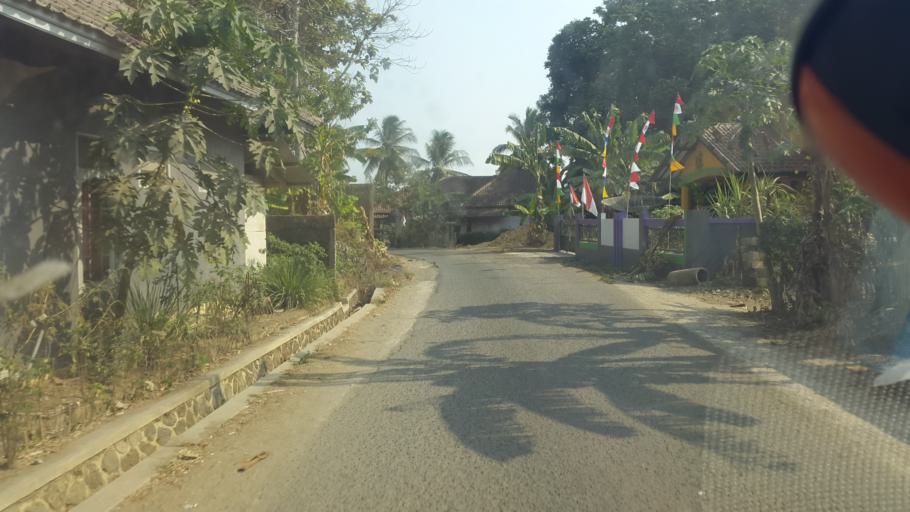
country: ID
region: West Java
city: Ciparay
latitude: -7.3024
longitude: 106.6221
